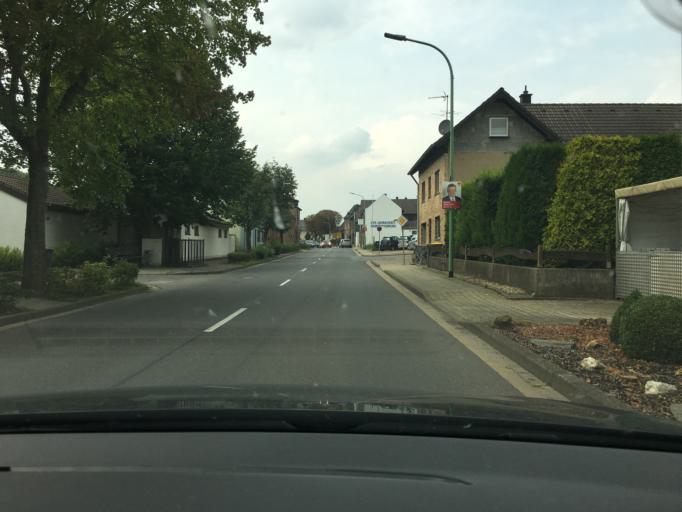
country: DE
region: North Rhine-Westphalia
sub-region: Regierungsbezirk Koln
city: Merzenich
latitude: 50.7914
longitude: 6.5741
